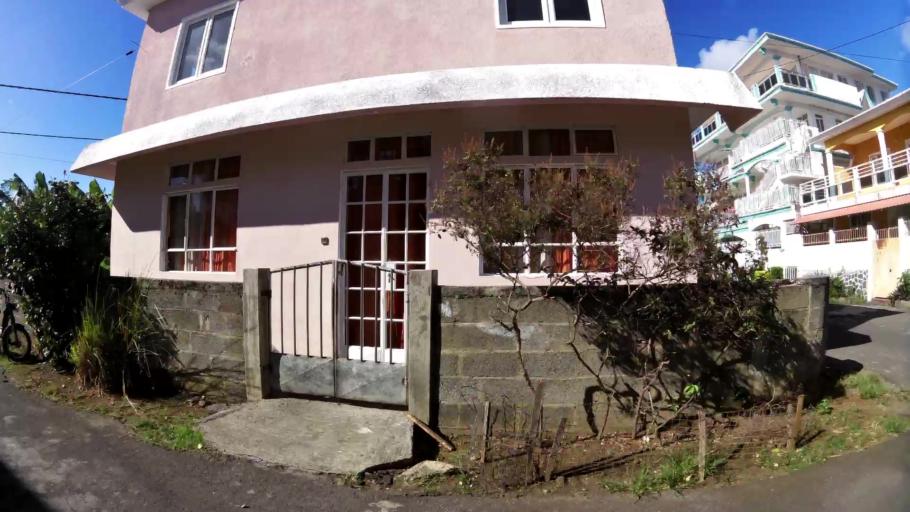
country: MU
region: Grand Port
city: Mahebourg
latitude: -20.4112
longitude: 57.7107
